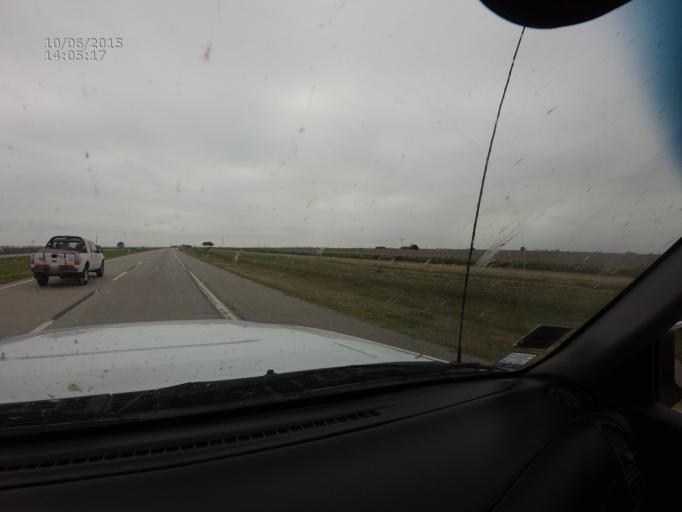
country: AR
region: Cordoba
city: Morrison
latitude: -32.5125
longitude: -62.9909
